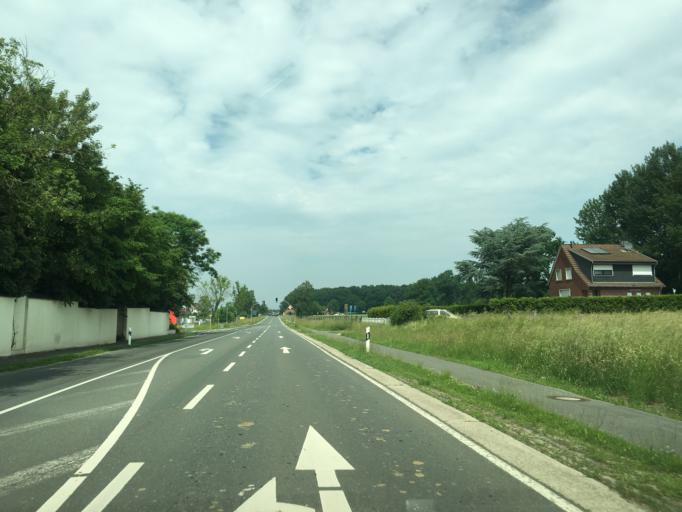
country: DE
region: North Rhine-Westphalia
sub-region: Regierungsbezirk Munster
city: Laer
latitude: 52.0973
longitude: 7.4132
